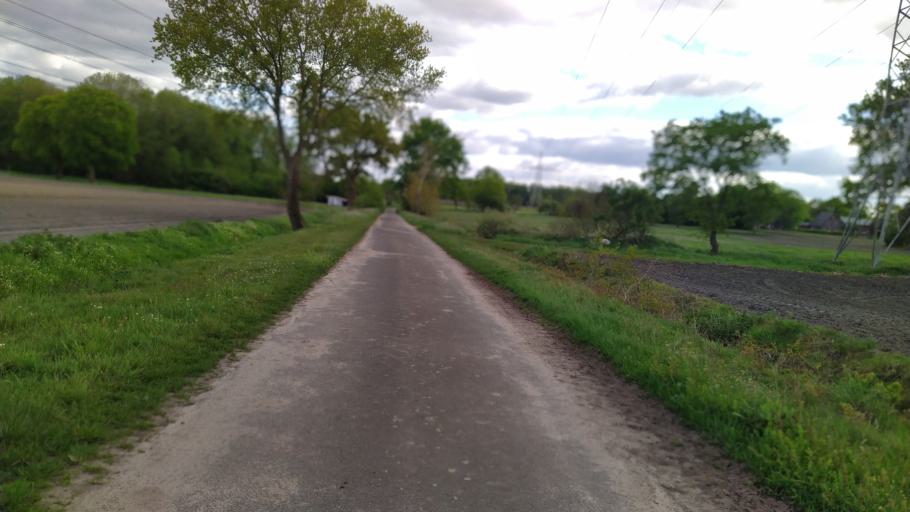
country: DE
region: Lower Saxony
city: Brest
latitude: 53.4259
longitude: 9.3906
